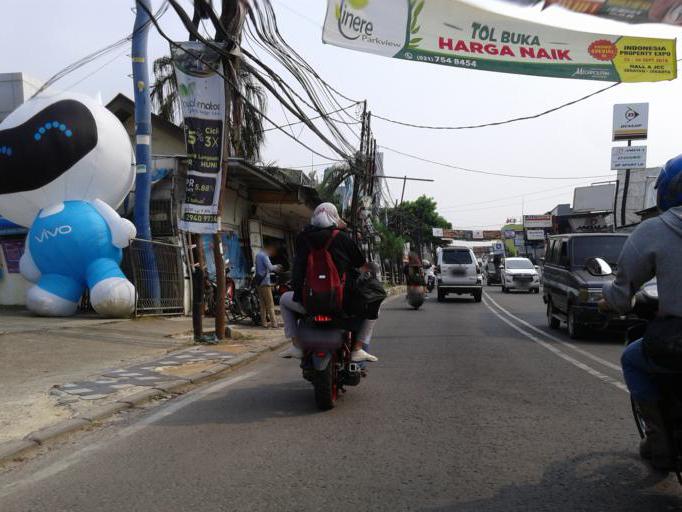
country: ID
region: West Java
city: Pamulang
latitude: -6.3303
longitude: 106.7841
